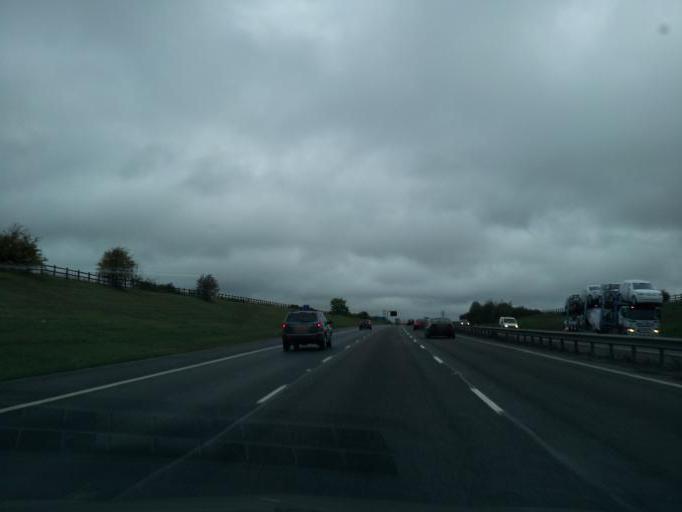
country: GB
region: England
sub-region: Oxfordshire
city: Bicester
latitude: 51.9096
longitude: -1.2054
